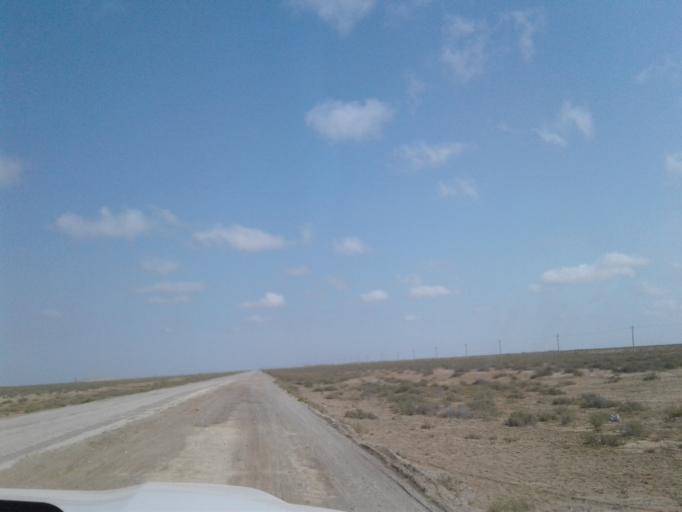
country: IR
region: Golestan
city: Gomishan
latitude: 37.6638
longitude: 53.9338
